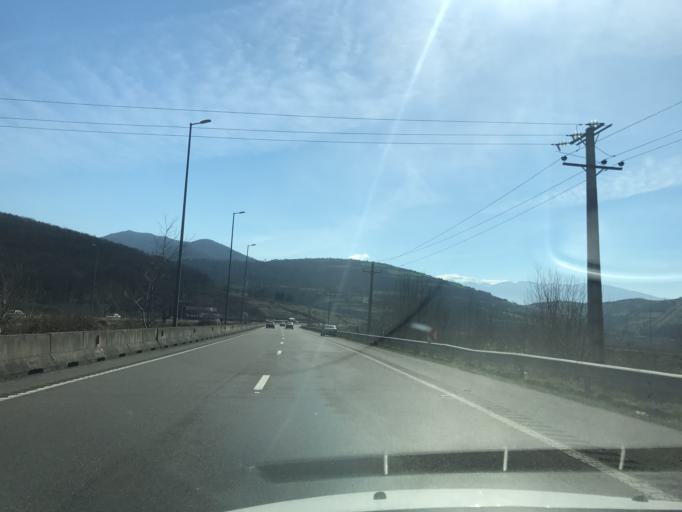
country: IR
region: Gilan
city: Pa'in-e Bazar-e Rudbar
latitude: 36.9492
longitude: 49.5487
